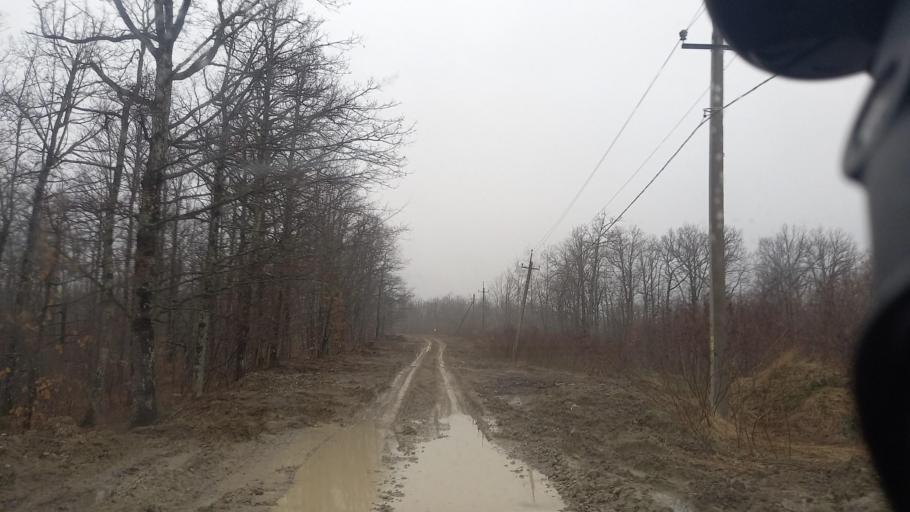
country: RU
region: Krasnodarskiy
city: Saratovskaya
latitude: 44.6166
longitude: 39.2362
